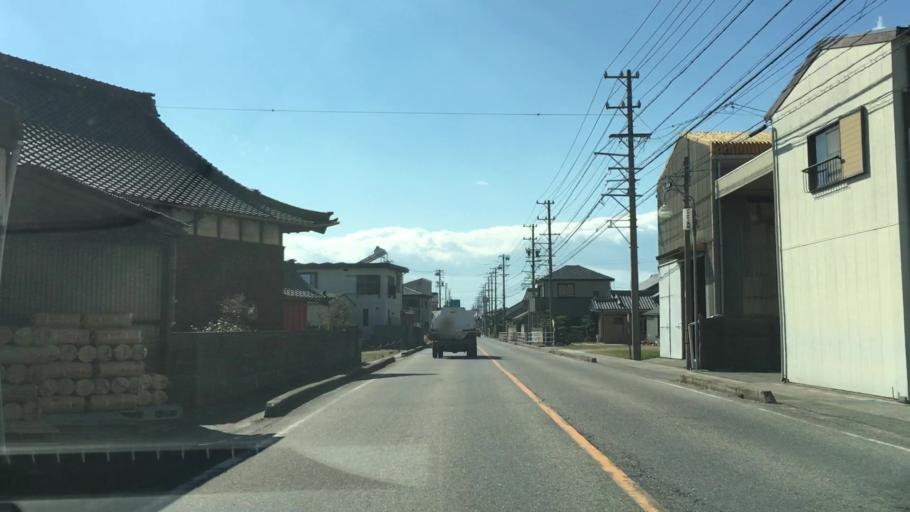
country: JP
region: Aichi
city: Ishiki
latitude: 34.7947
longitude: 137.1097
